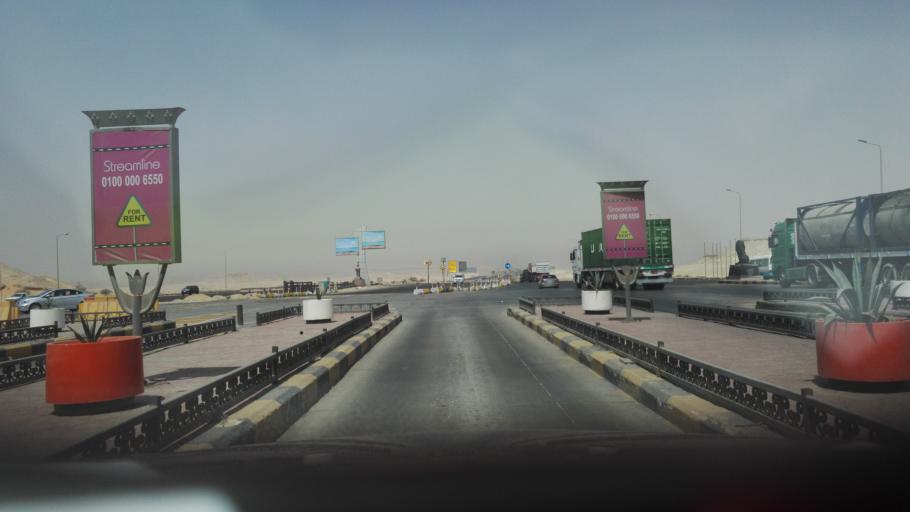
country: EG
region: As Suways
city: Ain Sukhna
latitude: 29.6578
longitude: 32.2569
